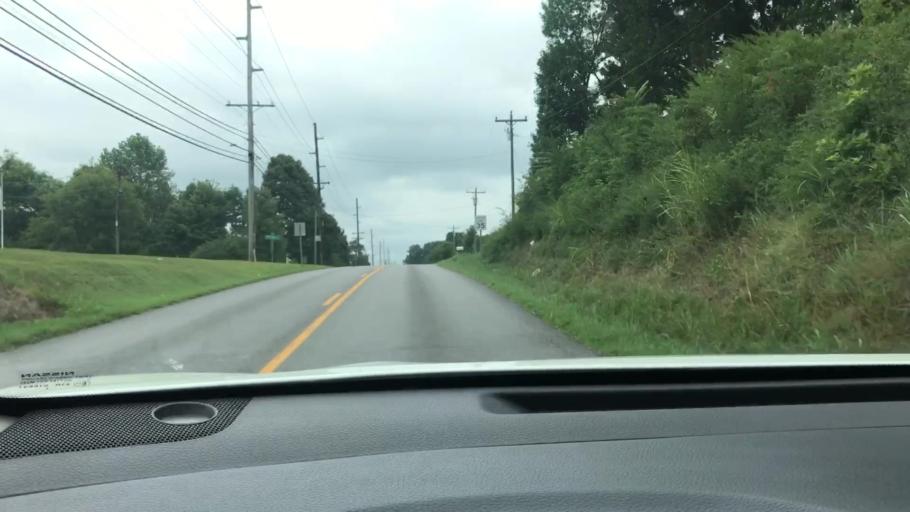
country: US
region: Kentucky
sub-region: Calloway County
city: Murray
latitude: 36.6242
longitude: -88.3020
